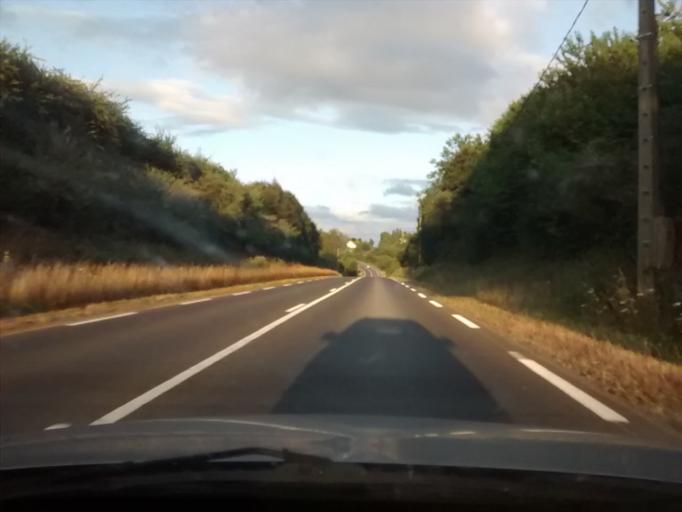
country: FR
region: Pays de la Loire
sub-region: Departement de la Sarthe
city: Saint-Saturnin
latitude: 48.0682
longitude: 0.1483
